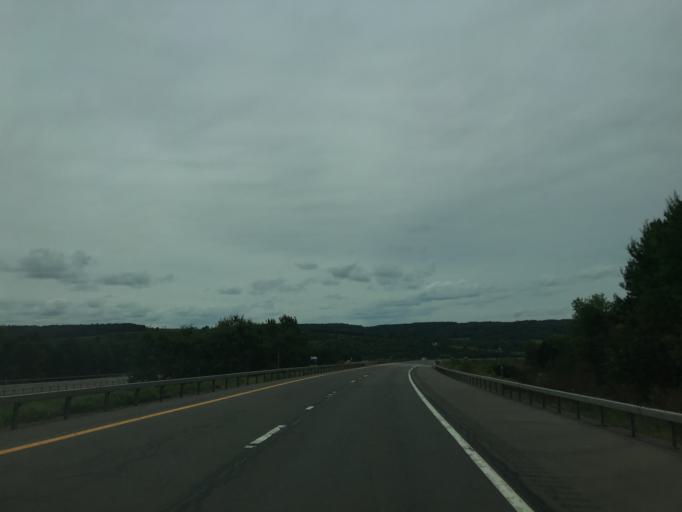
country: US
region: New York
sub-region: Chenango County
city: Greene
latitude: 42.1955
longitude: -75.6783
